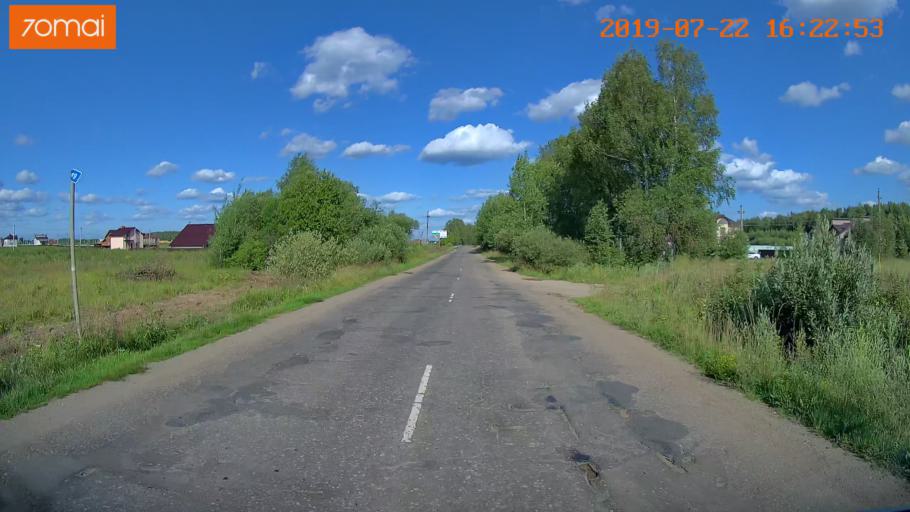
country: RU
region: Ivanovo
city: Novo-Talitsy
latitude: 57.0587
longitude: 40.8878
